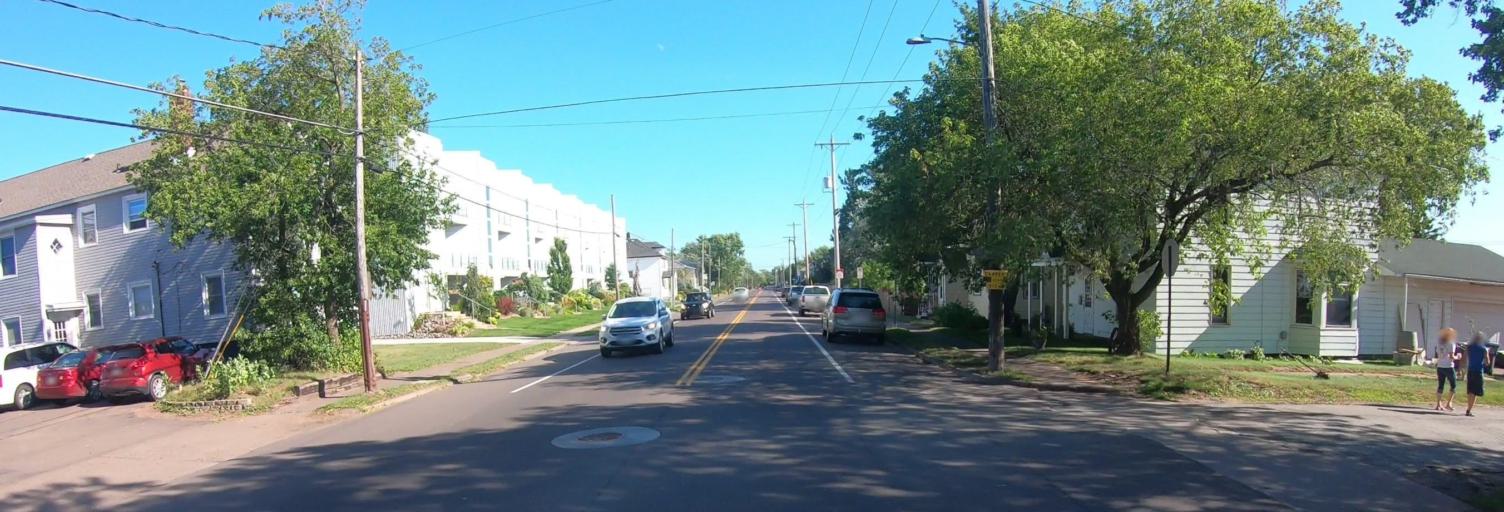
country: US
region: Minnesota
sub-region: Saint Louis County
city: Duluth
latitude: 46.7761
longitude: -92.0909
